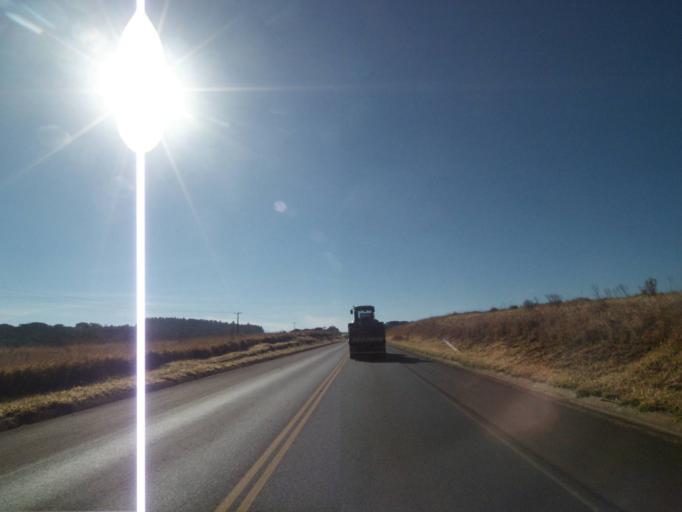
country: BR
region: Parana
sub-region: Tibagi
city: Tibagi
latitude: -24.4640
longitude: -50.4357
